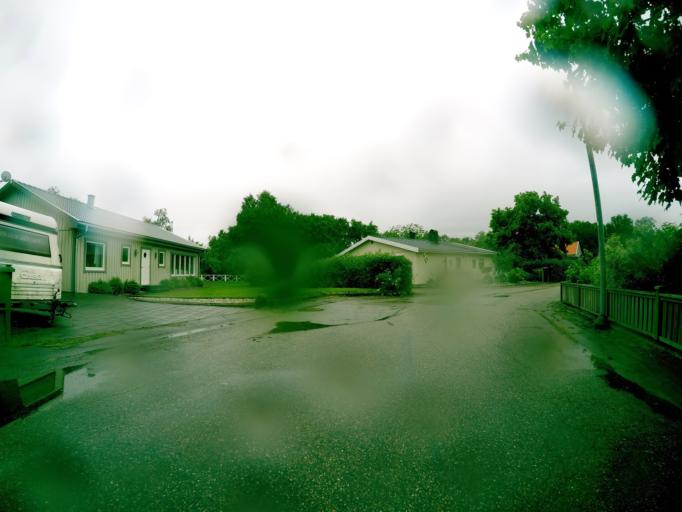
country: SE
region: Vaestra Goetaland
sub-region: Trollhattan
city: Sjuntorp
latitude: 58.1833
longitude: 12.2231
